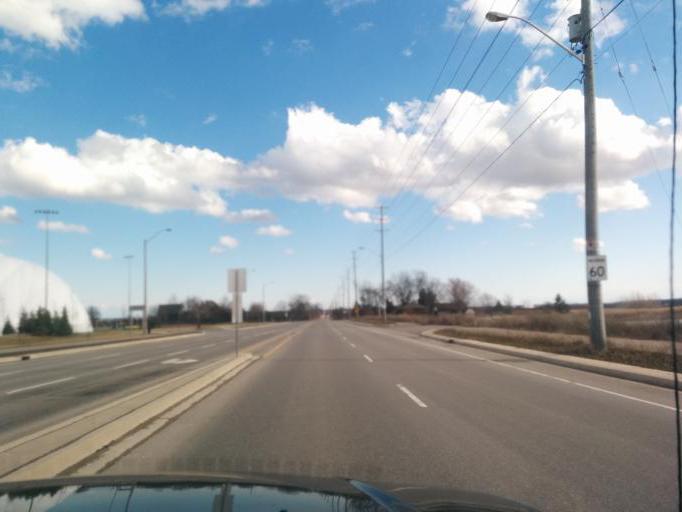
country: CA
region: Ontario
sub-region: Halton
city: Milton
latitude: 43.4863
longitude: -79.8582
